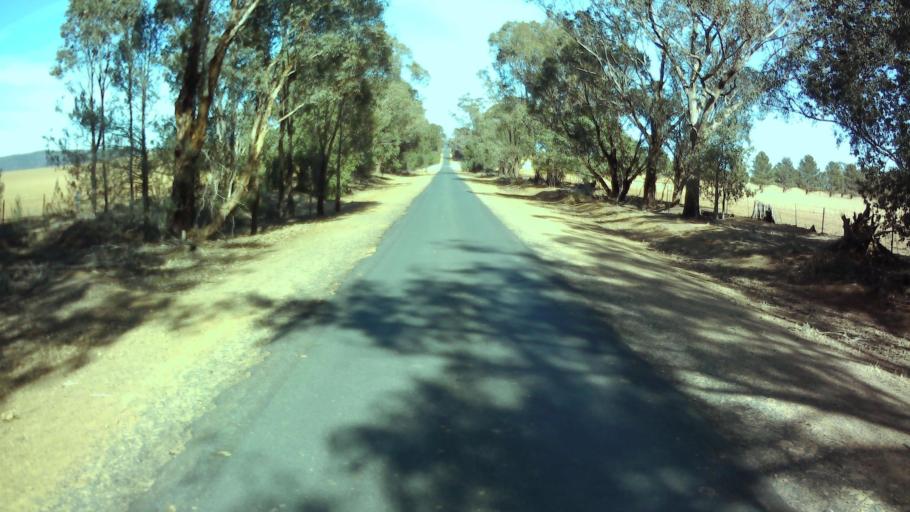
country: AU
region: New South Wales
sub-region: Weddin
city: Grenfell
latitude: -33.9067
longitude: 148.0717
